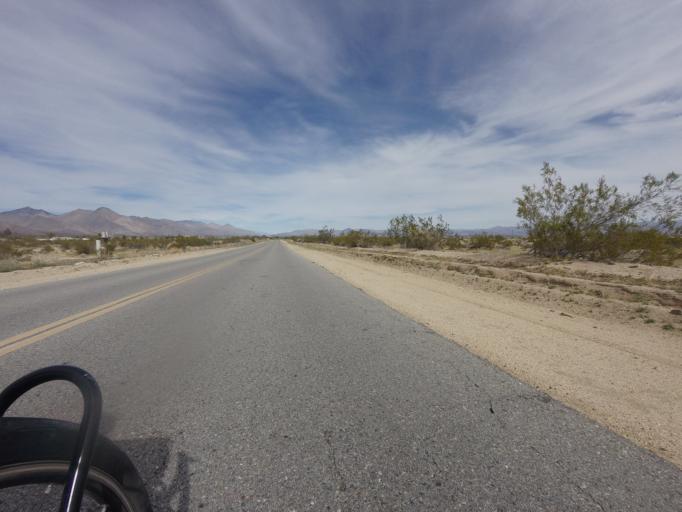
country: US
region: California
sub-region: Kern County
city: Inyokern
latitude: 35.7119
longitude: -117.8320
